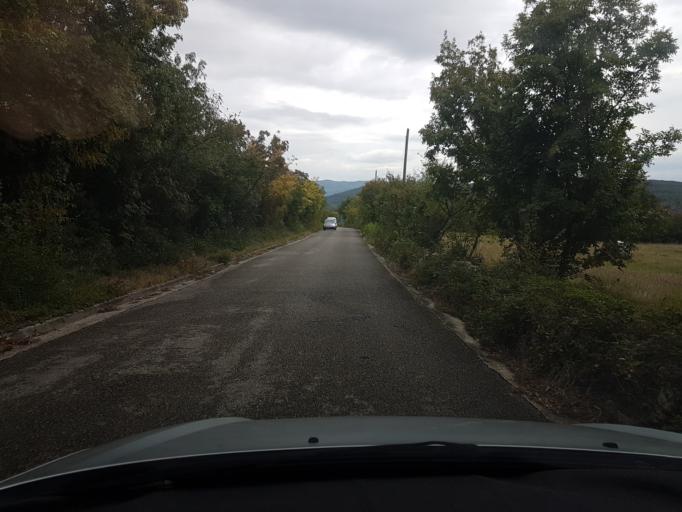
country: IT
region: Friuli Venezia Giulia
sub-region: Provincia di Gorizia
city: Doberdo del Lago
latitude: 45.8401
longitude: 13.5409
